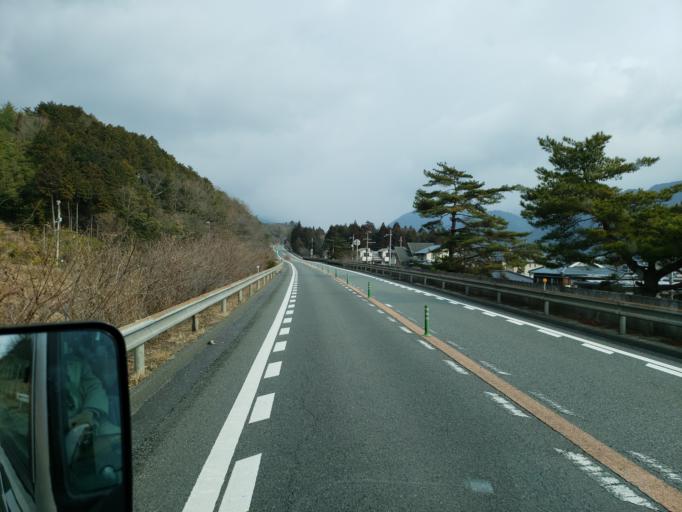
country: JP
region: Hyogo
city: Nishiwaki
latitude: 35.0717
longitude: 134.7699
